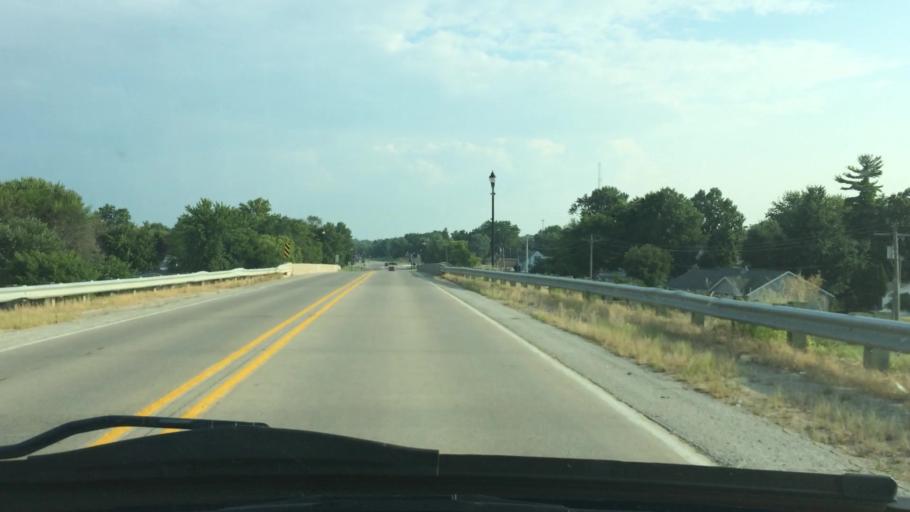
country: US
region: Iowa
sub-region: Henry County
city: Mount Pleasant
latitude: 40.9680
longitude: -91.5388
